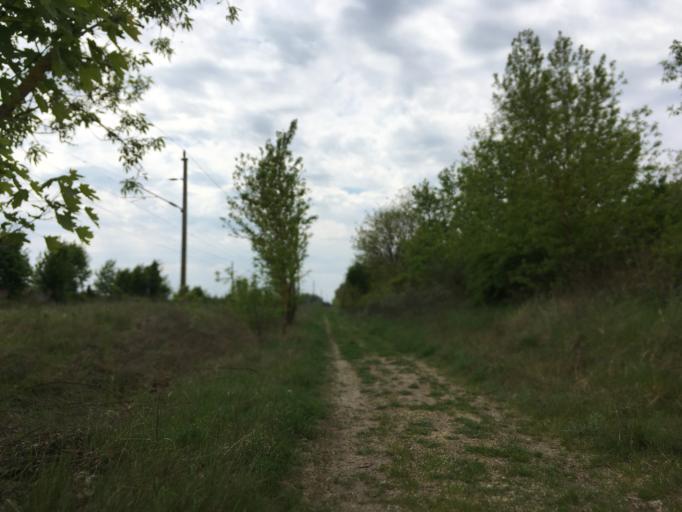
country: DE
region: Brandenburg
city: Bernau bei Berlin
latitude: 52.6920
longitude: 13.6101
